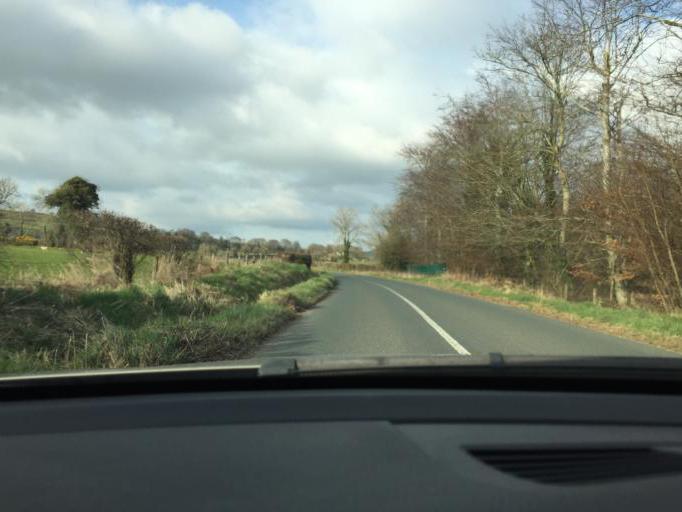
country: IE
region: Leinster
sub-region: Wicklow
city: Valleymount
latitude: 53.1237
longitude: -6.5329
